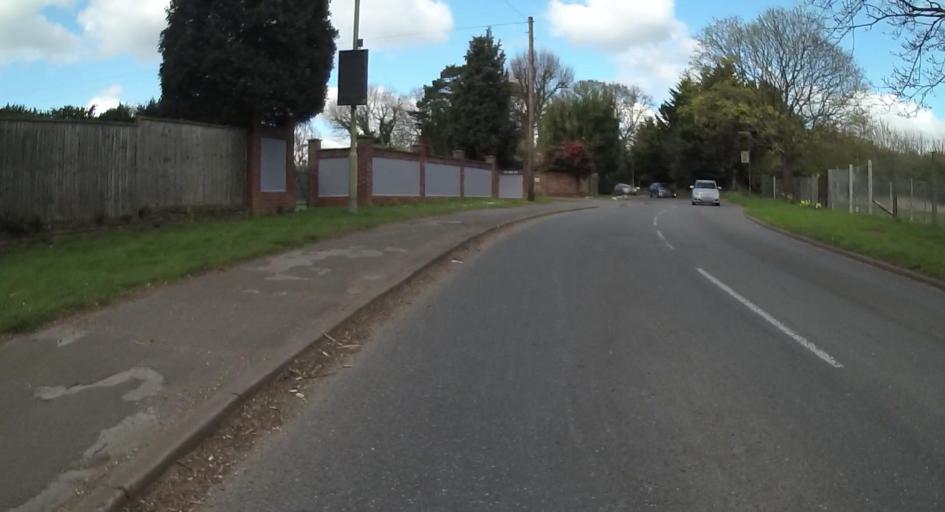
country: GB
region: England
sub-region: Surrey
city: West Byfleet
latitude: 51.3507
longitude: -0.5137
